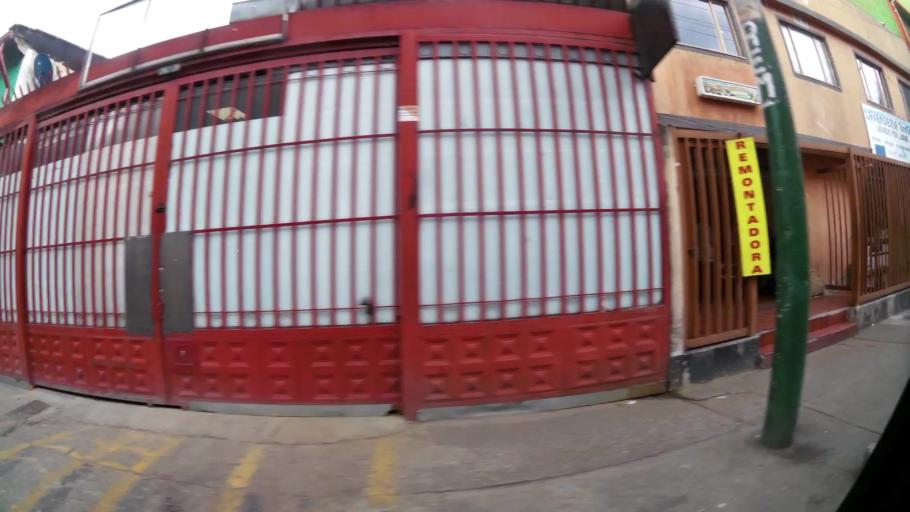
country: CO
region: Cundinamarca
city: La Calera
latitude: 4.7417
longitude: -74.0356
